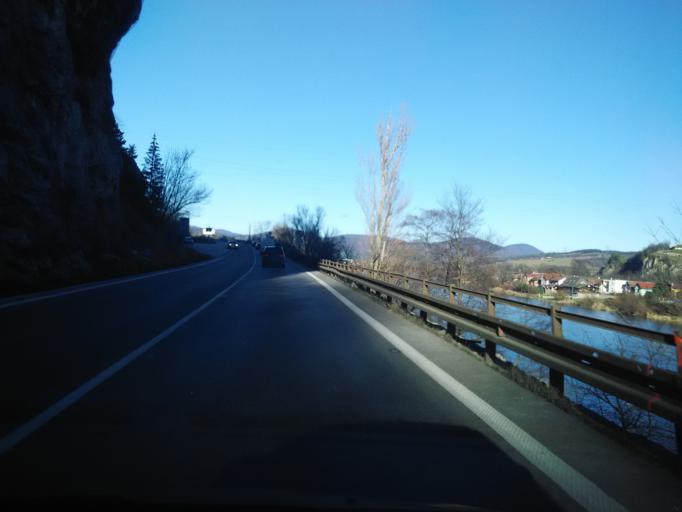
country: SK
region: Zilinsky
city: Krasnany
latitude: 49.1755
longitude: 18.8633
